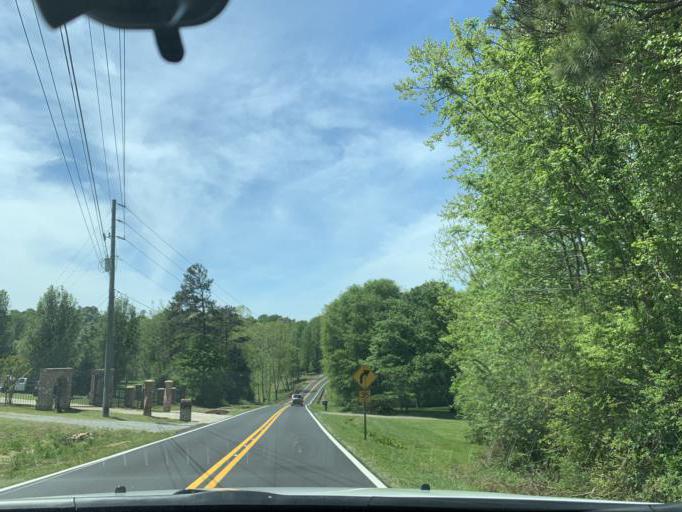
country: US
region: Georgia
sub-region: Forsyth County
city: Cumming
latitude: 34.2645
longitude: -84.0519
